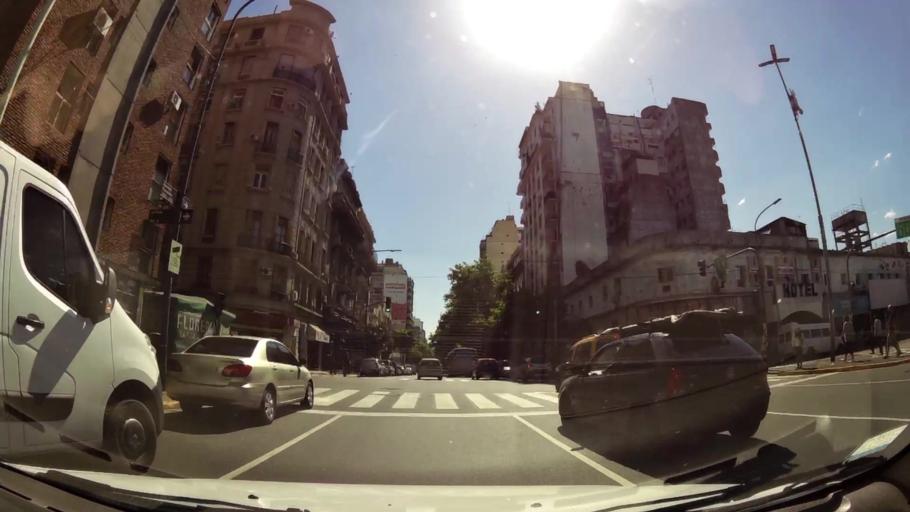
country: AR
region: Buenos Aires F.D.
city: Buenos Aires
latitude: -34.6103
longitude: -58.4087
